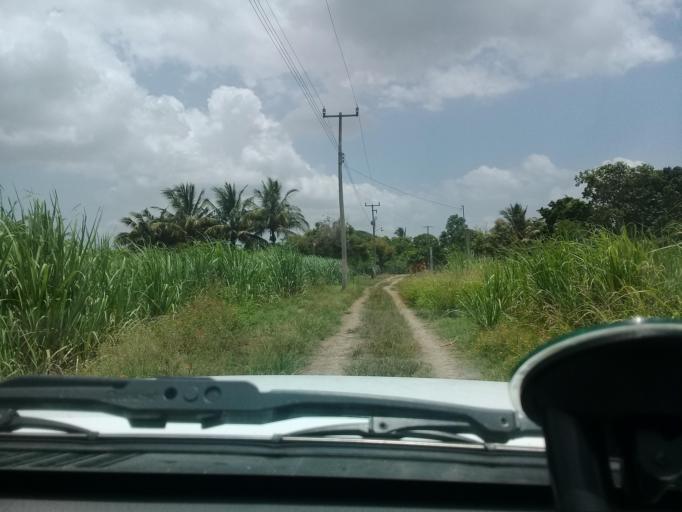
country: MX
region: Veracruz
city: Moralillo
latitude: 22.1367
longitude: -98.0404
